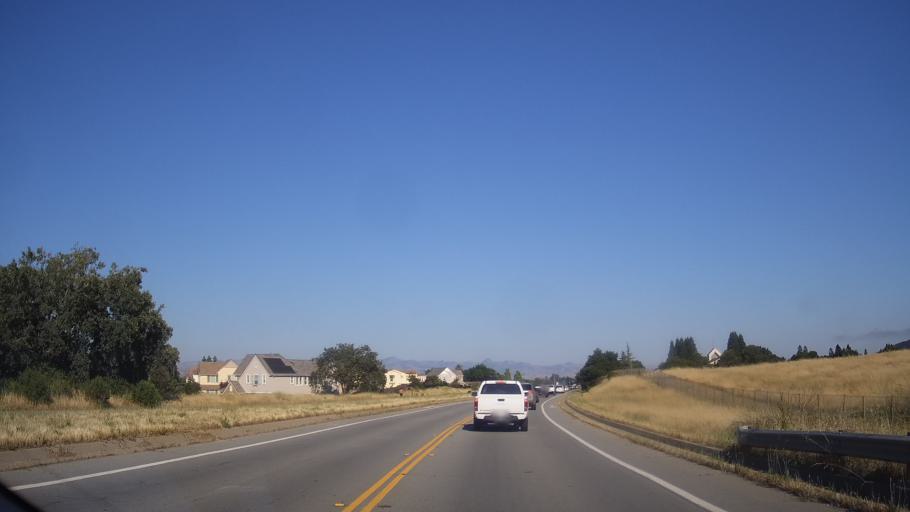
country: US
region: California
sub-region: Santa Clara County
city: Gilroy
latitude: 36.9862
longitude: -121.5808
